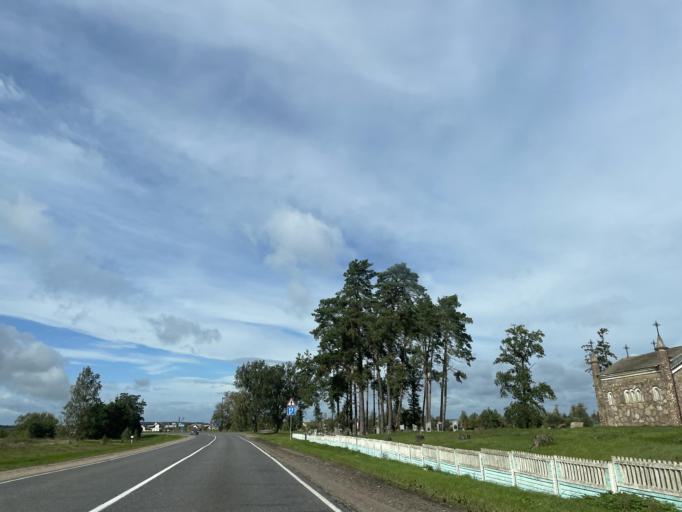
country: BY
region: Brest
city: Kosava
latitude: 52.7470
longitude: 25.1747
